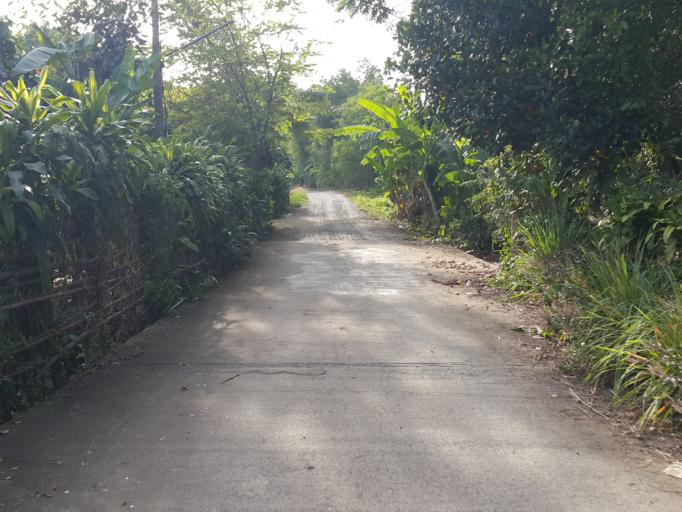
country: TH
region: Chiang Mai
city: San Kamphaeng
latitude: 18.8047
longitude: 99.1237
